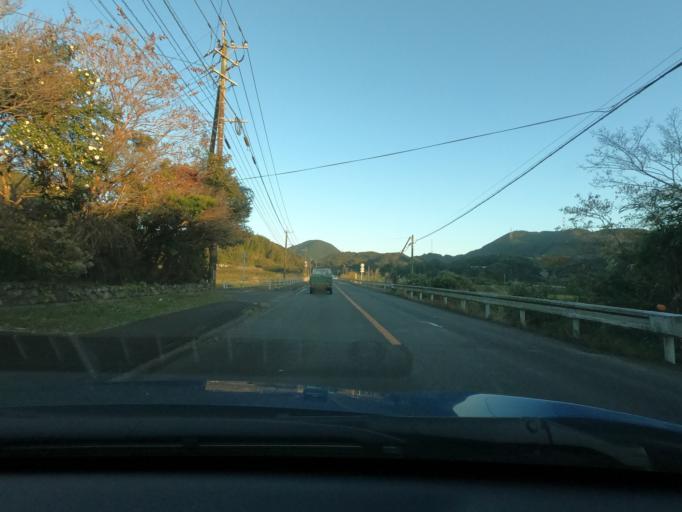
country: JP
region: Kagoshima
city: Satsumasendai
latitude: 31.7912
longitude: 130.4601
